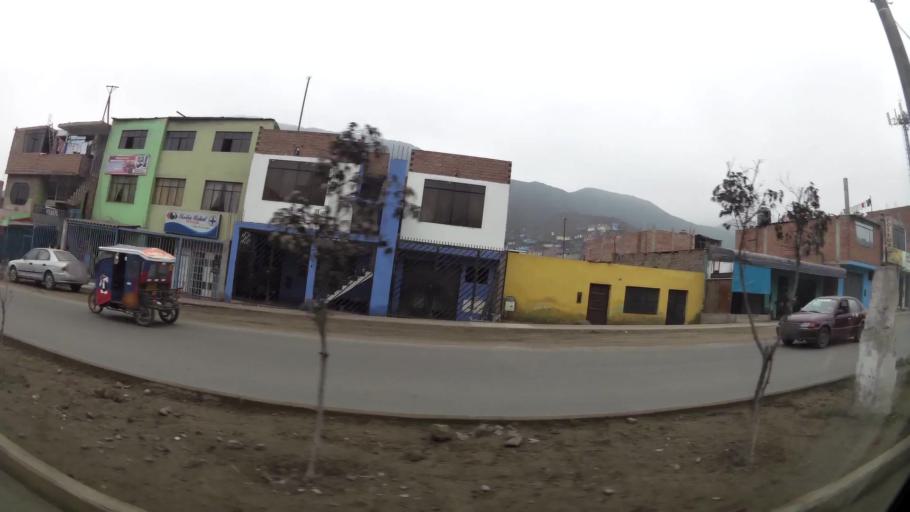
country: PE
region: Lima
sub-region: Lima
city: Urb. Santo Domingo
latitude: -11.9132
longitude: -77.0252
